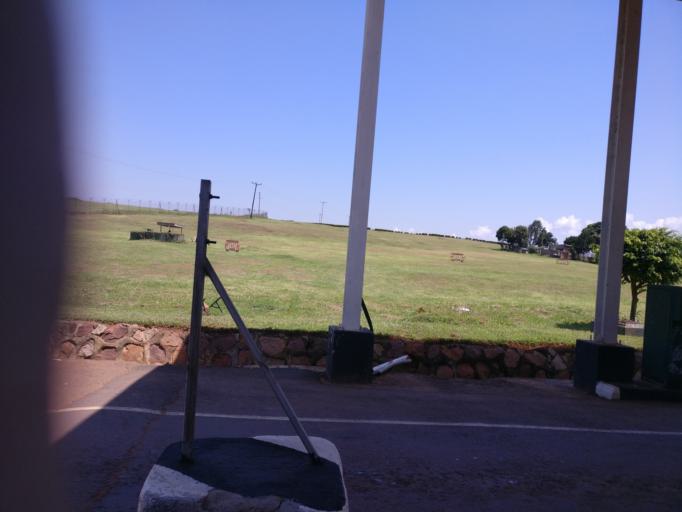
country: UG
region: Central Region
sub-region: Wakiso District
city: Entebbe
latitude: 0.0425
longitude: 32.4478
